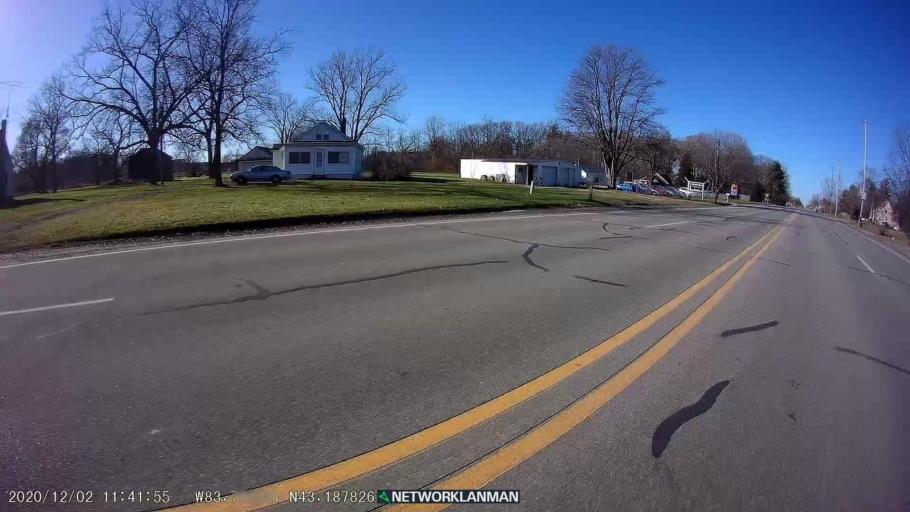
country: US
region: Michigan
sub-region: Genesee County
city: Clio
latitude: 43.1881
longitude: -83.7225
